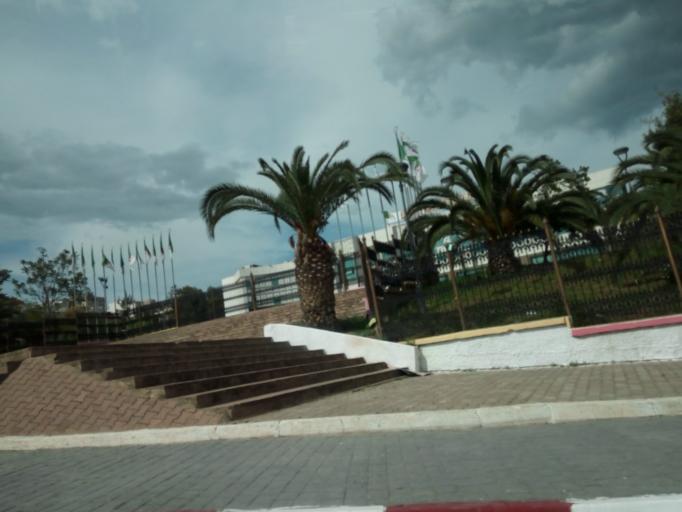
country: DZ
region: Constantine
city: Constantine
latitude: 36.3509
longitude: 6.6088
